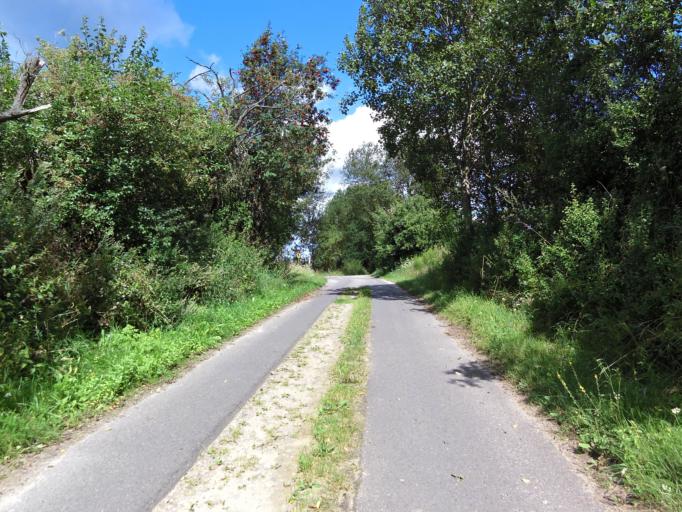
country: DE
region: Brandenburg
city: Lychen
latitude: 53.2497
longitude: 13.3598
